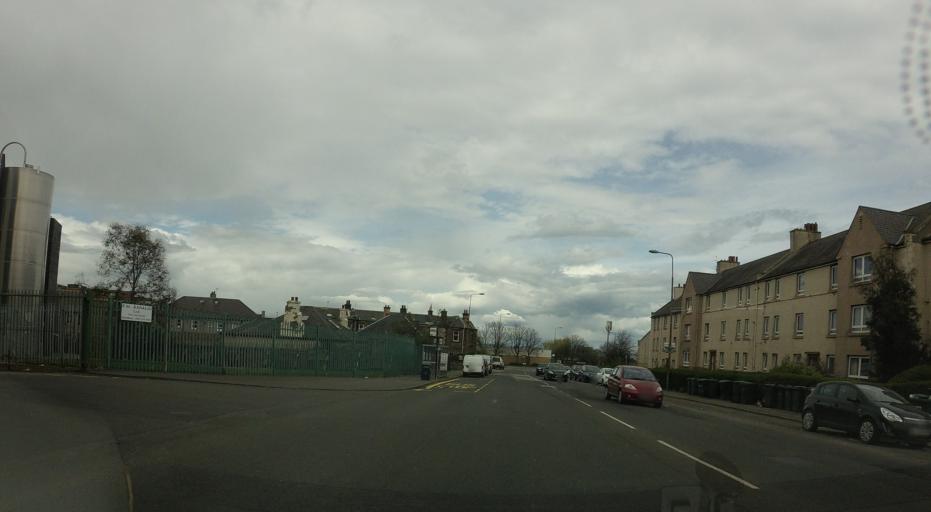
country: GB
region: Scotland
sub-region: Edinburgh
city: Edinburgh
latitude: 55.9796
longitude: -3.2309
